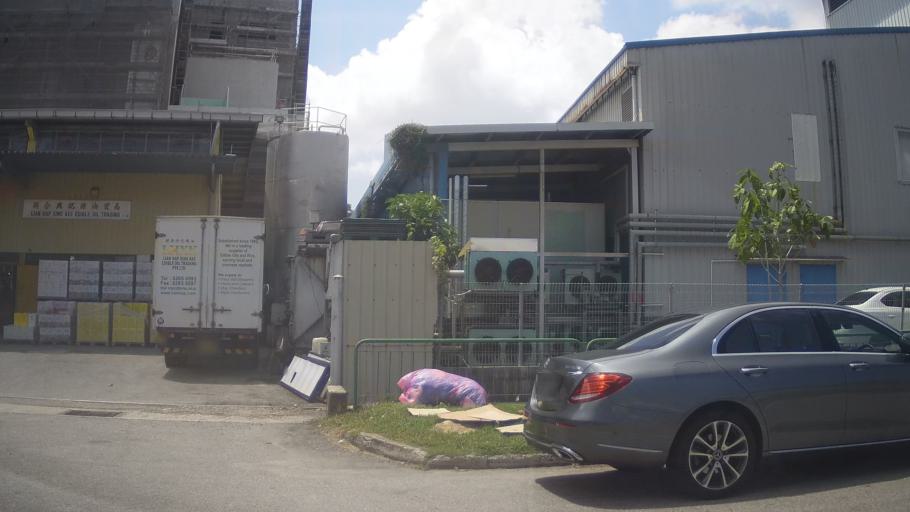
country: MY
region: Johor
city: Johor Bahru
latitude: 1.3370
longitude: 103.7134
